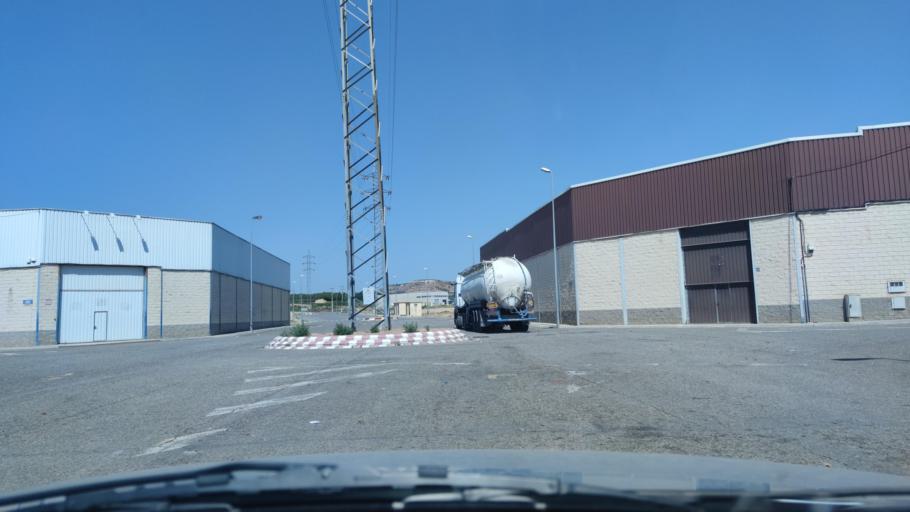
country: ES
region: Catalonia
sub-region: Provincia de Lleida
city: Torrefarrera
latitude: 41.6653
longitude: 0.6019
